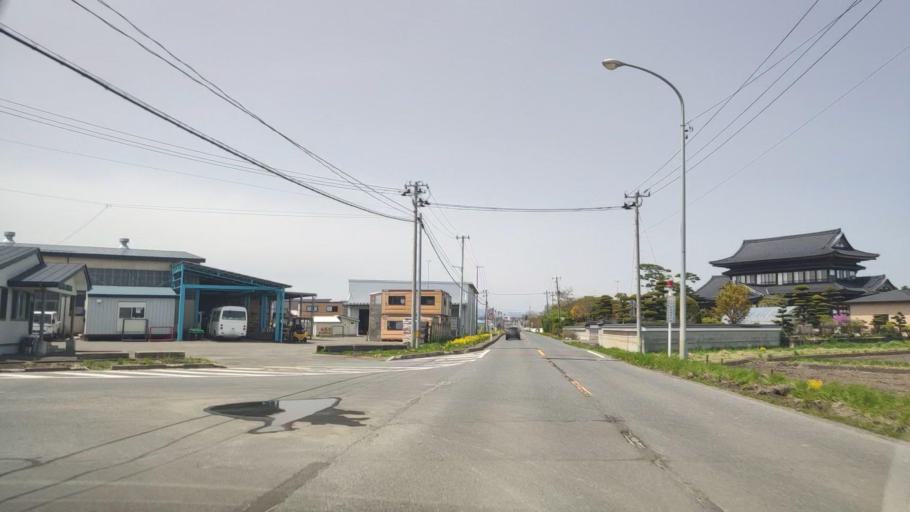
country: JP
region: Aomori
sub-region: Misawa Shi
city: Inuotose
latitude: 40.6032
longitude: 141.2975
